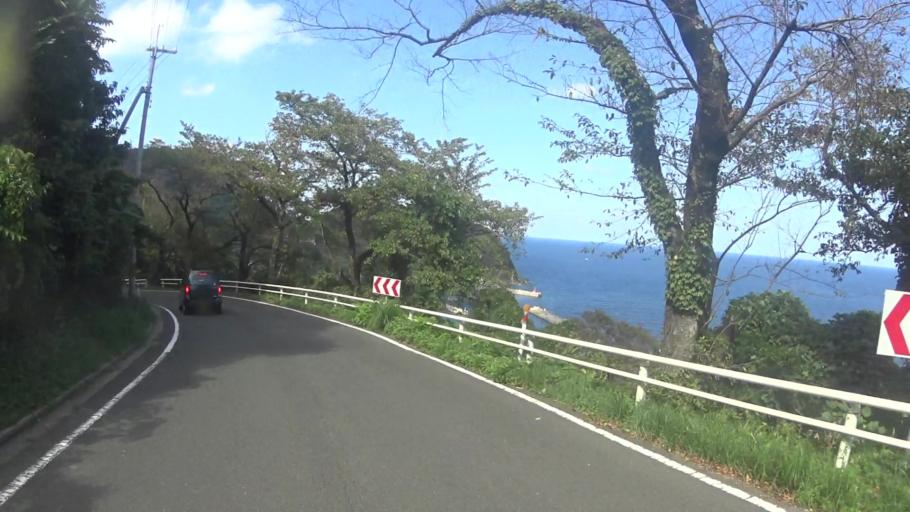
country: JP
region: Kyoto
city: Miyazu
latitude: 35.7478
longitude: 135.2522
